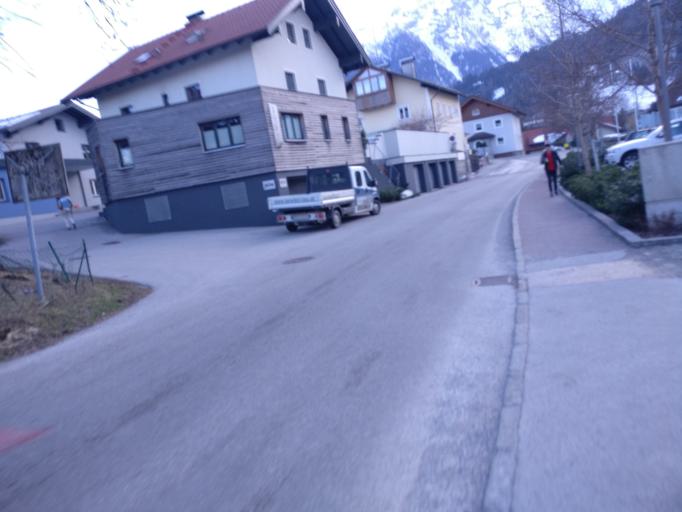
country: AT
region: Salzburg
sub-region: Politischer Bezirk Hallein
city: Kuchl
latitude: 47.6282
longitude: 13.1453
